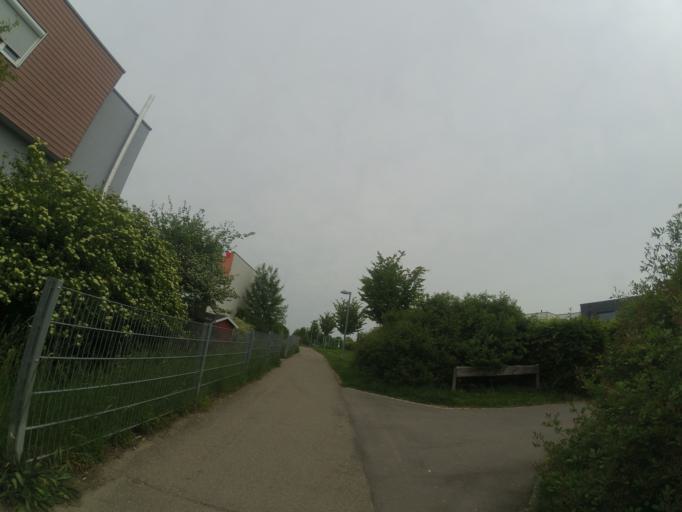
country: DE
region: Baden-Wuerttemberg
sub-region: Tuebingen Region
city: Ulm
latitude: 48.3493
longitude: 9.9817
